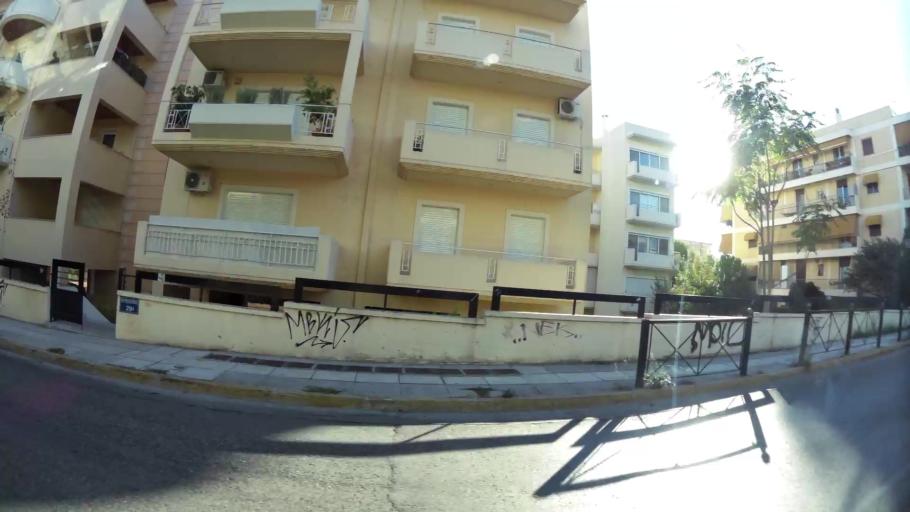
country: GR
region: Attica
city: Pefki
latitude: 38.0590
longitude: 23.7987
